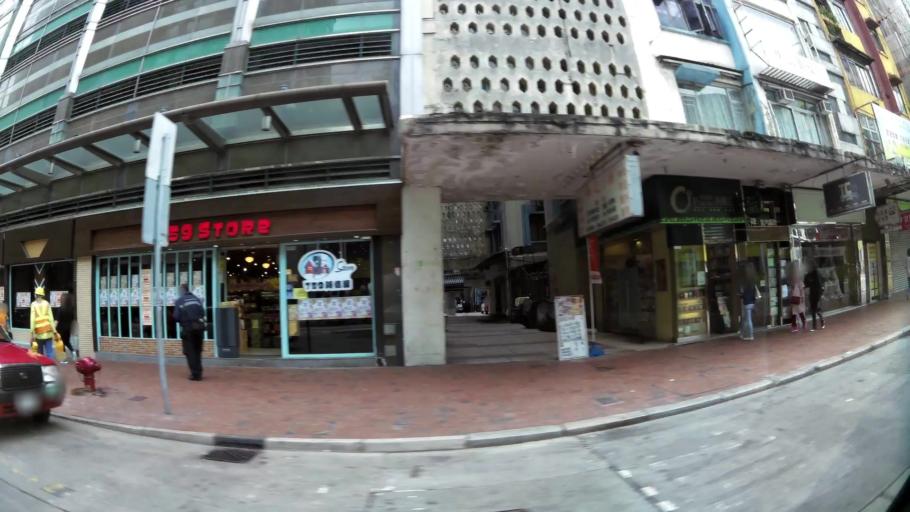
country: HK
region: Wanchai
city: Wan Chai
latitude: 22.2893
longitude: 114.2098
